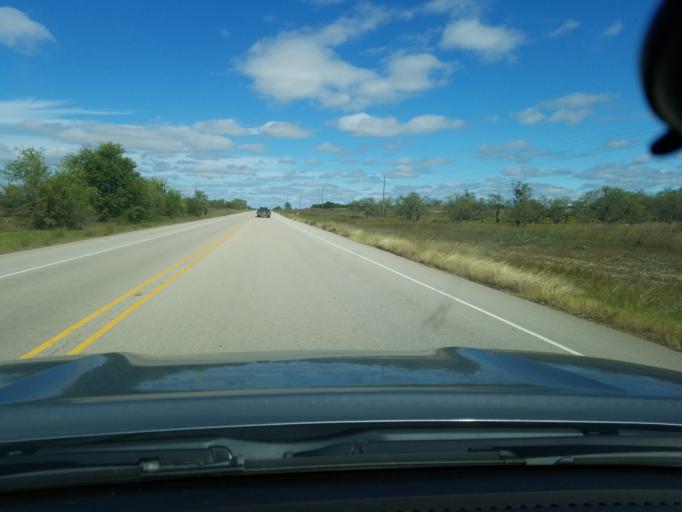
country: US
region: Texas
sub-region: Hamilton County
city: Hamilton
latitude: 31.6603
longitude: -98.1422
